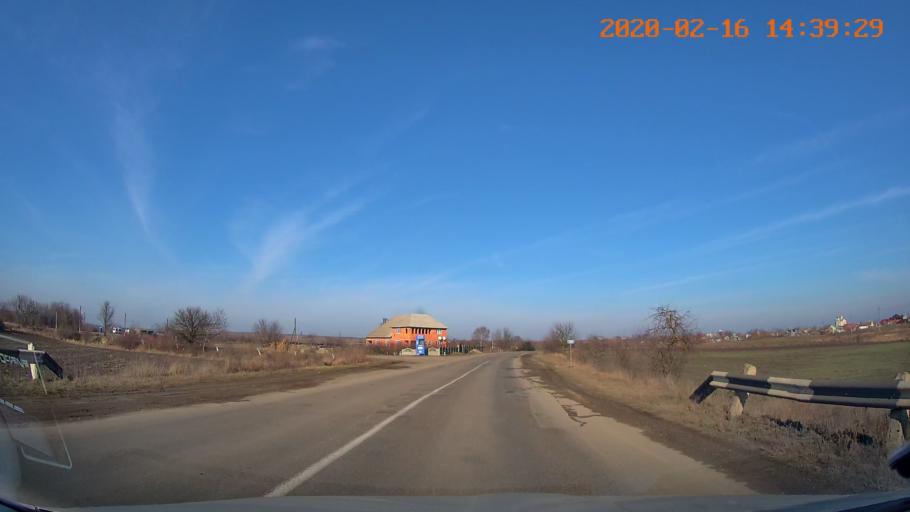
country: RO
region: Botosani
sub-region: Comuna Darabani
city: Bajura
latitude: 48.2436
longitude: 26.5493
